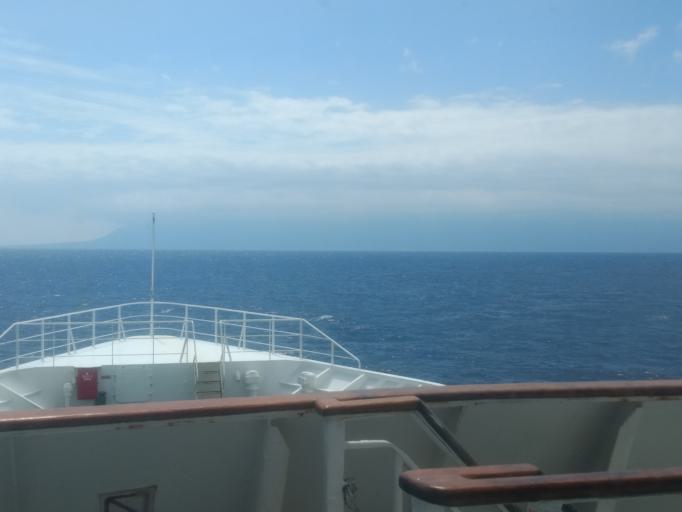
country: JP
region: Kagoshima
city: Nishinoomote
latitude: 30.6099
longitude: 130.6200
